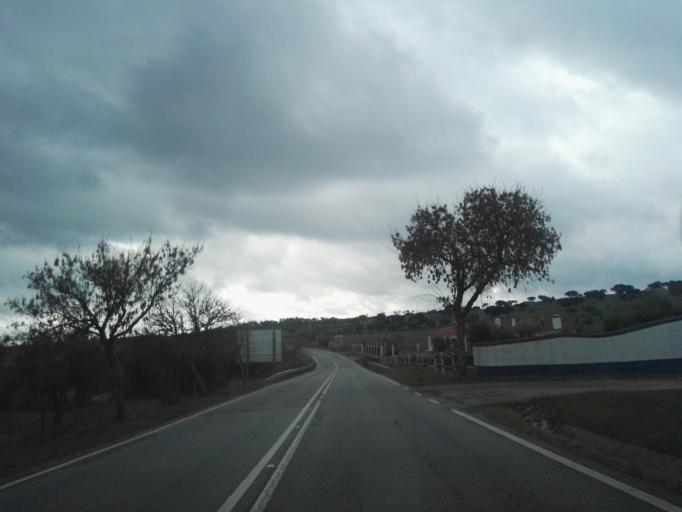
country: PT
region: Portalegre
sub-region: Arronches
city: Arronches
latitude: 39.1221
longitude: -7.2954
